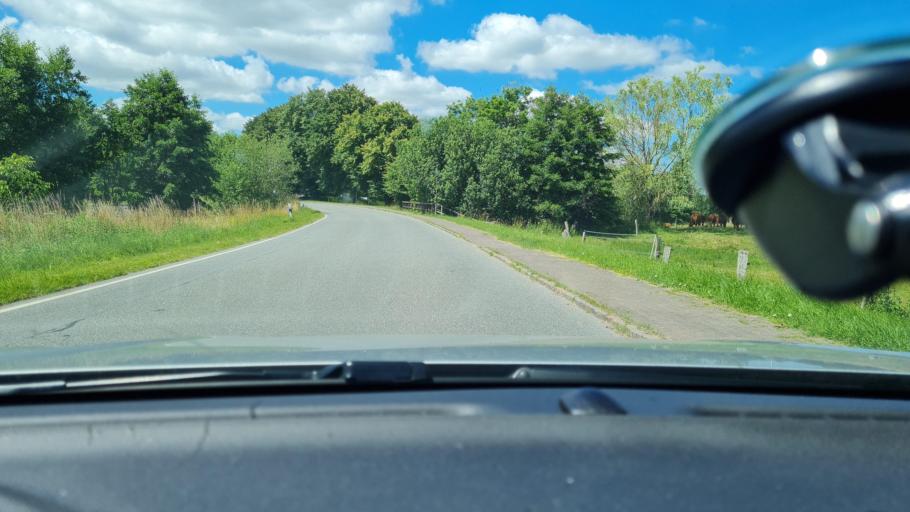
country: DE
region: Schleswig-Holstein
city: Rabenkirchen-Fauluck
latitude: 54.5930
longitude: 9.8660
